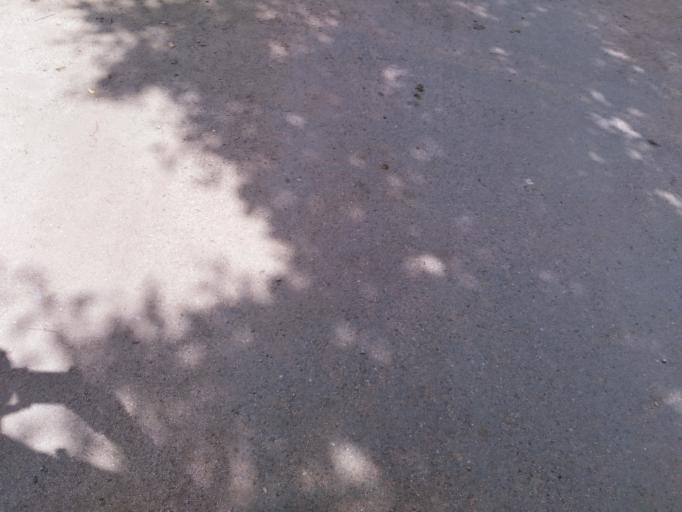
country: RU
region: Bashkortostan
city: Akhunovo
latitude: 54.2088
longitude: 59.6042
